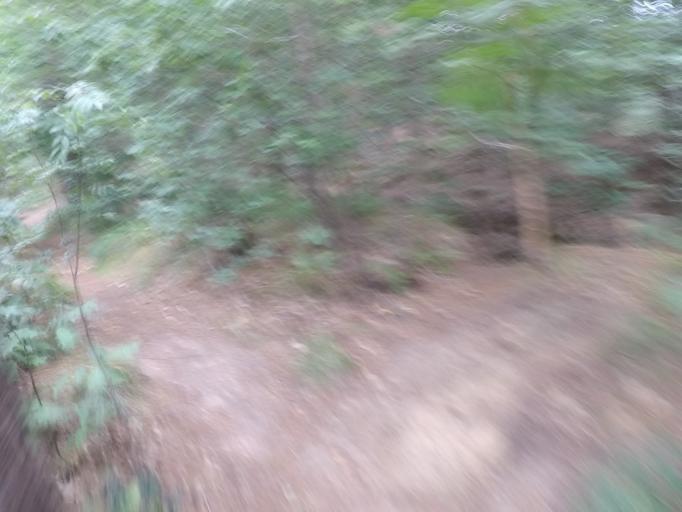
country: BE
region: Flanders
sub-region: Provincie Antwerpen
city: Kasterlee
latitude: 51.2420
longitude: 4.9487
